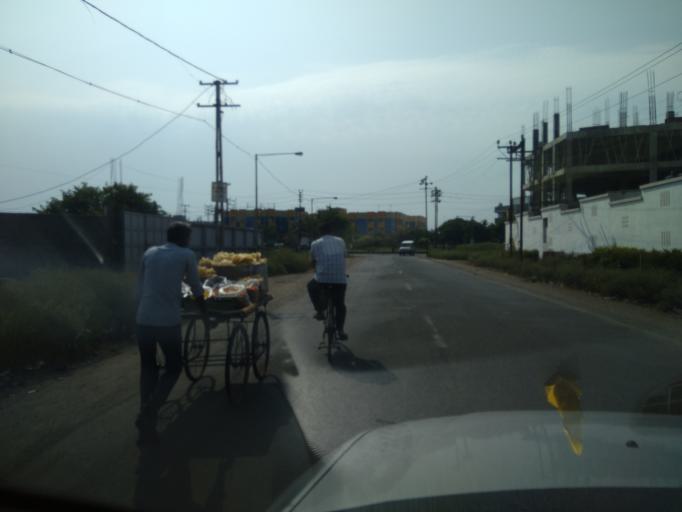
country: IN
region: Gujarat
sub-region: Jamnagar
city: Jamnagar
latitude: 22.4205
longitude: 70.0498
